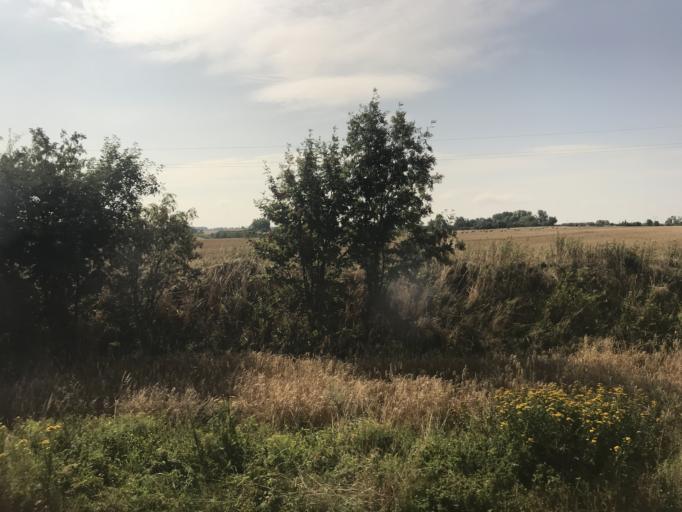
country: PL
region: Kujawsko-Pomorskie
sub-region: Powiat swiecki
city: Pruszcz
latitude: 53.3641
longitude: 18.2490
